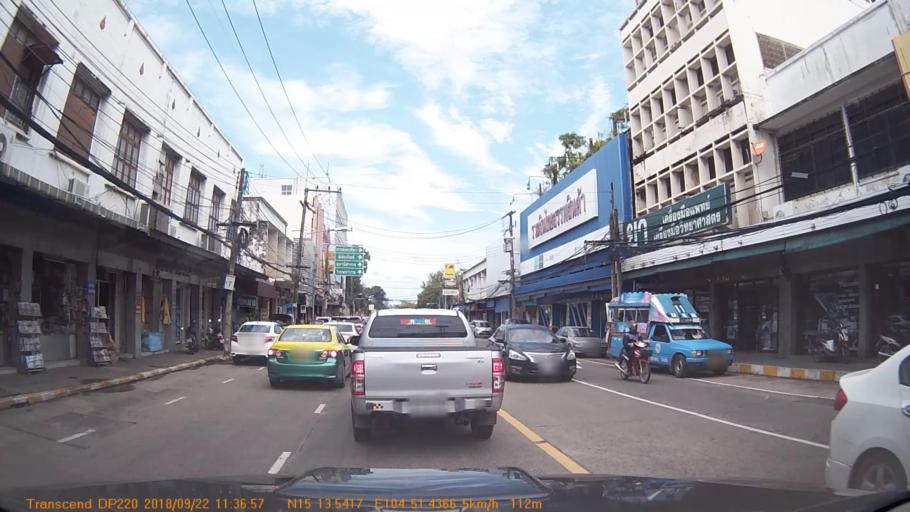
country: TH
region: Changwat Ubon Ratchathani
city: Ubon Ratchathani
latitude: 15.2257
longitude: 104.8573
